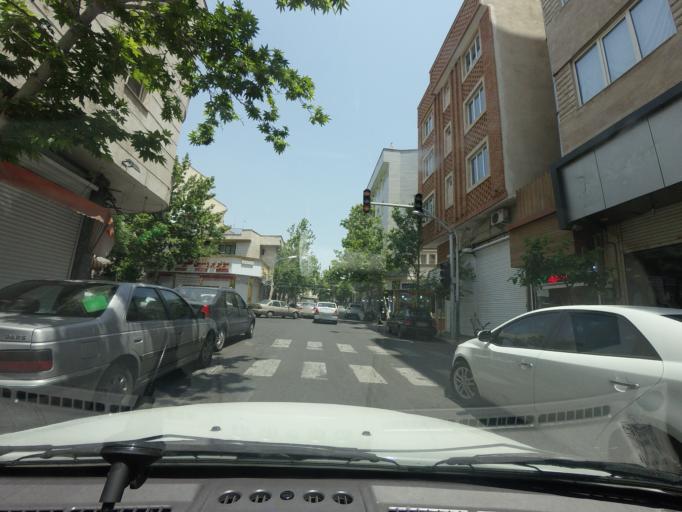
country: IR
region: Tehran
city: Tehran
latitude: 35.6937
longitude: 51.4420
